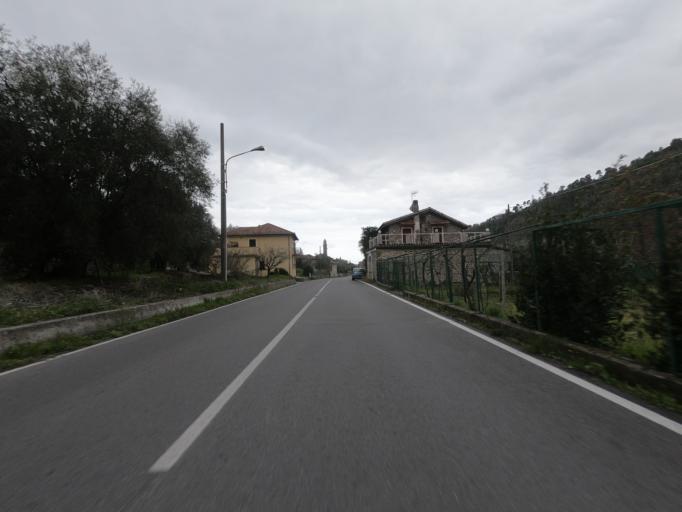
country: IT
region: Liguria
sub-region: Provincia di Savona
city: Villafranca
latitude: 43.9986
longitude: 8.1108
